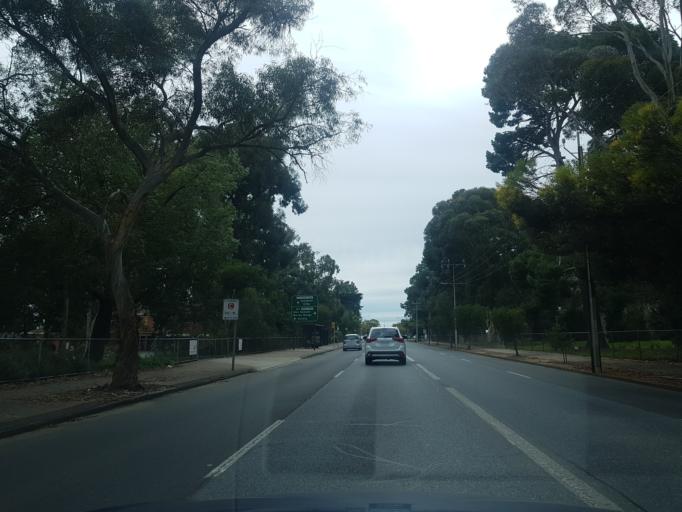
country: AU
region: South Australia
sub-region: Mitcham
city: Mitcham
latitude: -34.9670
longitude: 138.6266
